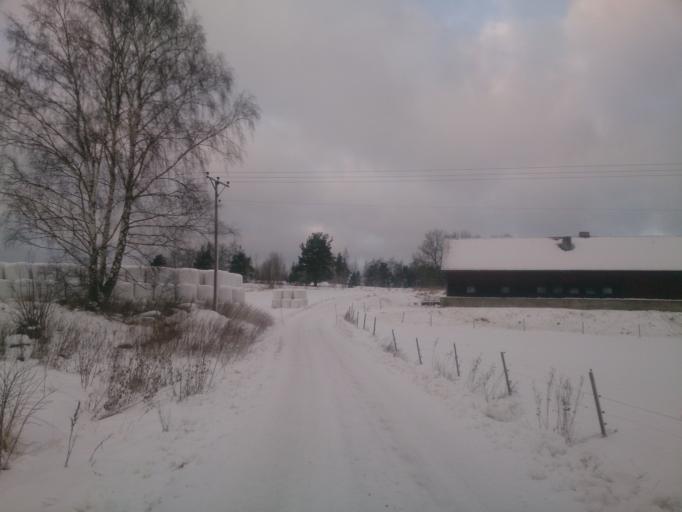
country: SE
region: OEstergoetland
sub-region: Atvidabergs Kommun
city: Atvidaberg
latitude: 58.2216
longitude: 15.9894
